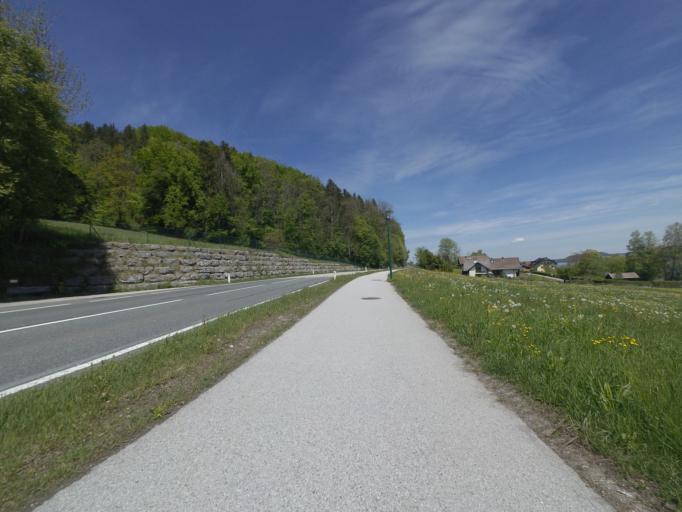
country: AT
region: Salzburg
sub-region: Politischer Bezirk Salzburg-Umgebung
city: Obertrum am See
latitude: 47.9432
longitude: 13.0685
